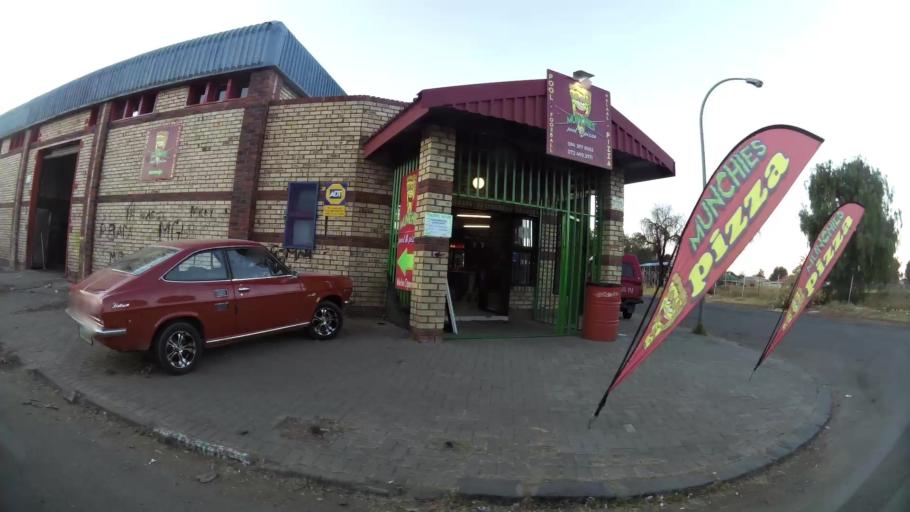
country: ZA
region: Northern Cape
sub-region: Frances Baard District Municipality
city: Kimberley
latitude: -28.7296
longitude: 24.7663
